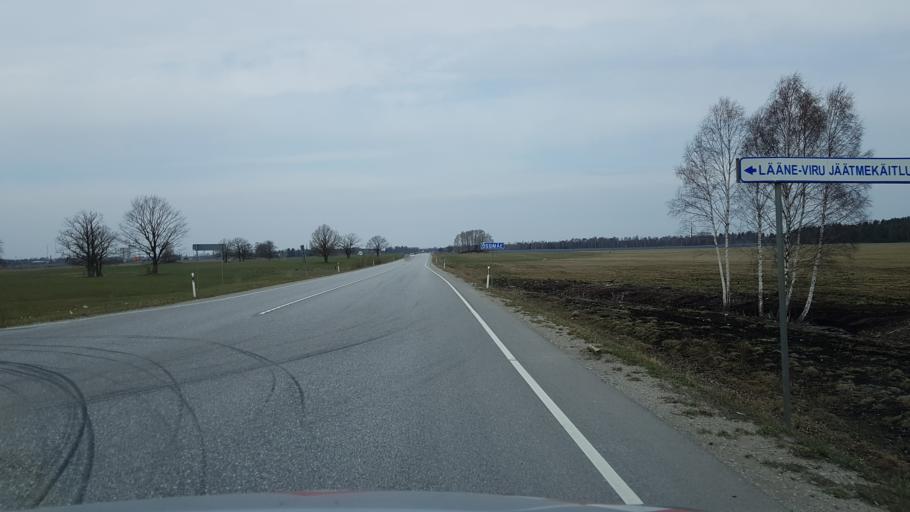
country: EE
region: Laeaene-Virumaa
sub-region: Someru vald
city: Someru
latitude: 59.3455
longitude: 26.4081
